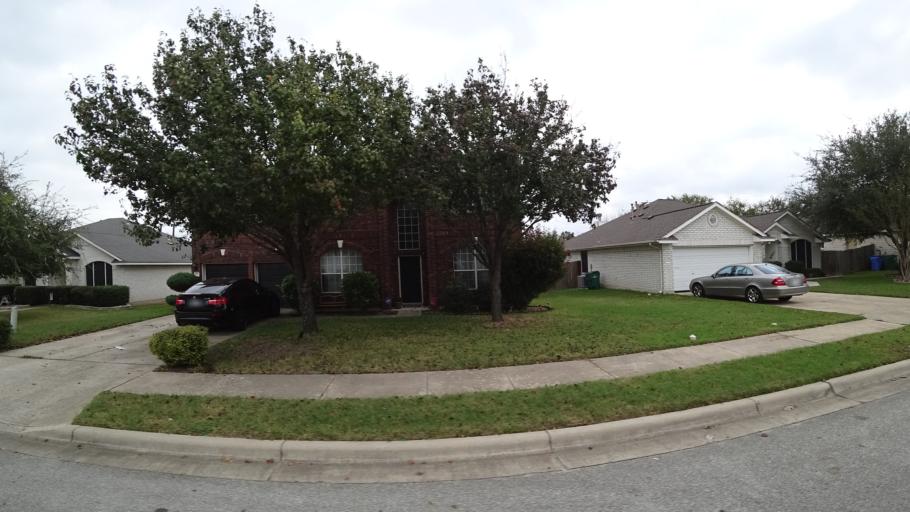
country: US
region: Texas
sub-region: Travis County
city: Pflugerville
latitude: 30.4403
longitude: -97.6049
